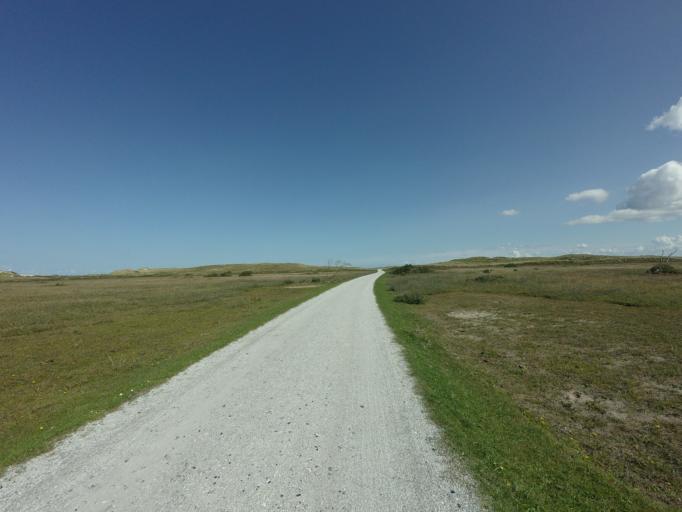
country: NL
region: Friesland
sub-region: Gemeente Terschelling
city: West-Terschelling
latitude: 53.4196
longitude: 5.3947
